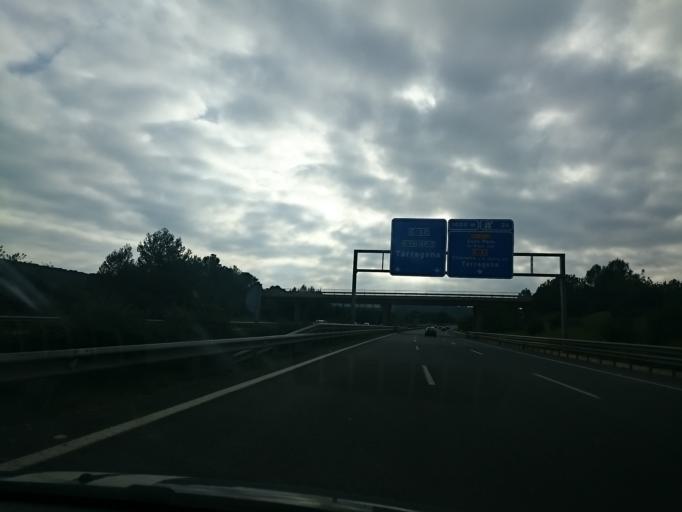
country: ES
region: Catalonia
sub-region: Provincia de Barcelona
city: Sant Pere de Ribes
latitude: 41.2482
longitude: 1.7812
